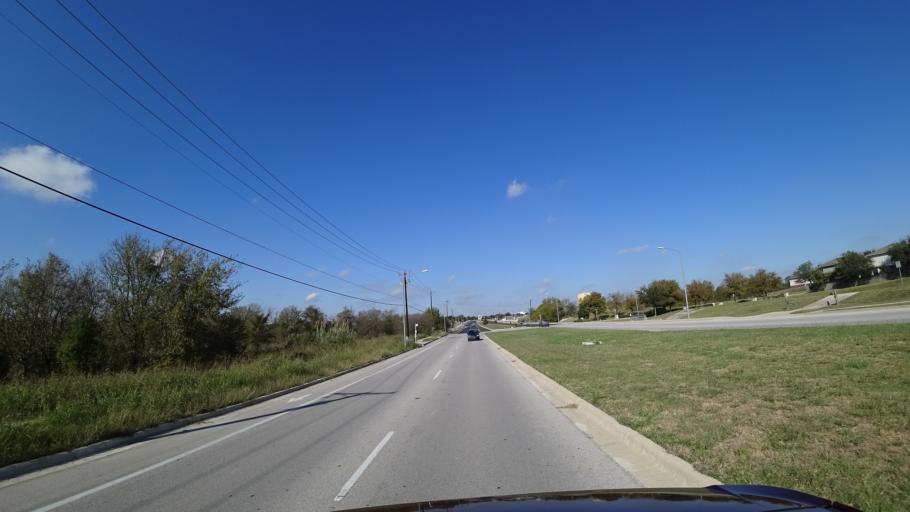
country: US
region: Texas
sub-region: Travis County
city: Wells Branch
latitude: 30.4378
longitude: -97.6584
